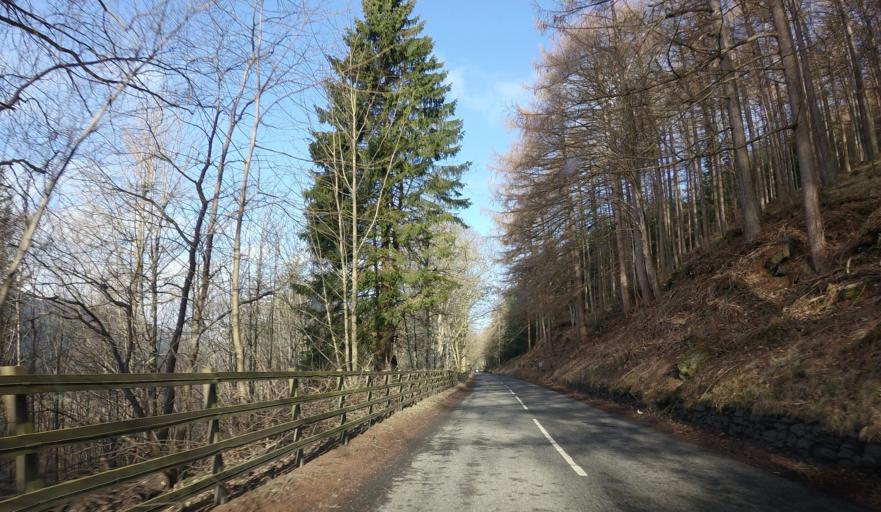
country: GB
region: Scotland
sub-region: Perth and Kinross
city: Bankfoot
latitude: 56.5779
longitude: -3.6184
